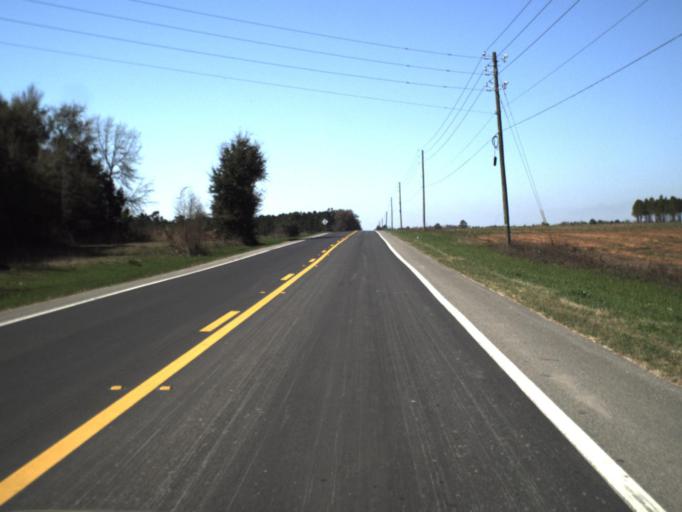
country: US
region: Florida
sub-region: Jackson County
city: Marianna
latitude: 30.6620
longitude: -85.1647
